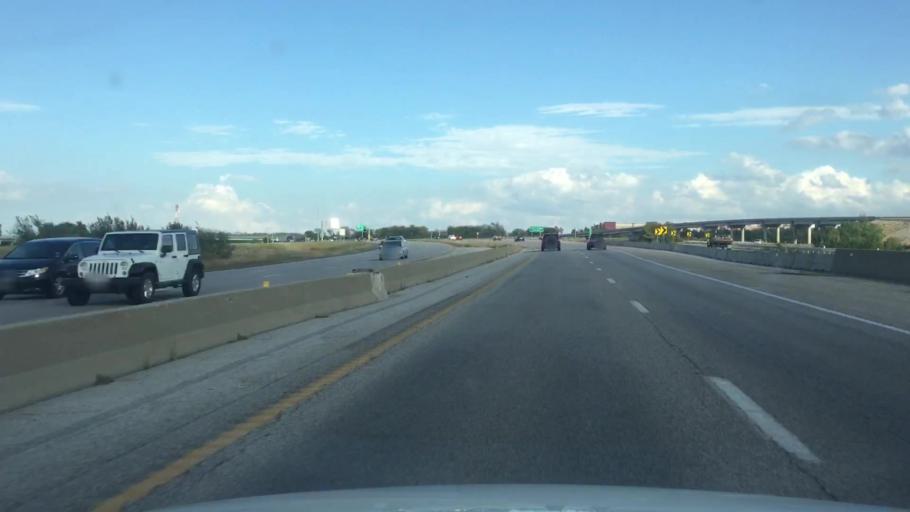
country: US
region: Missouri
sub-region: Jackson County
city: Lees Summit
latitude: 38.9338
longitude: -94.4115
